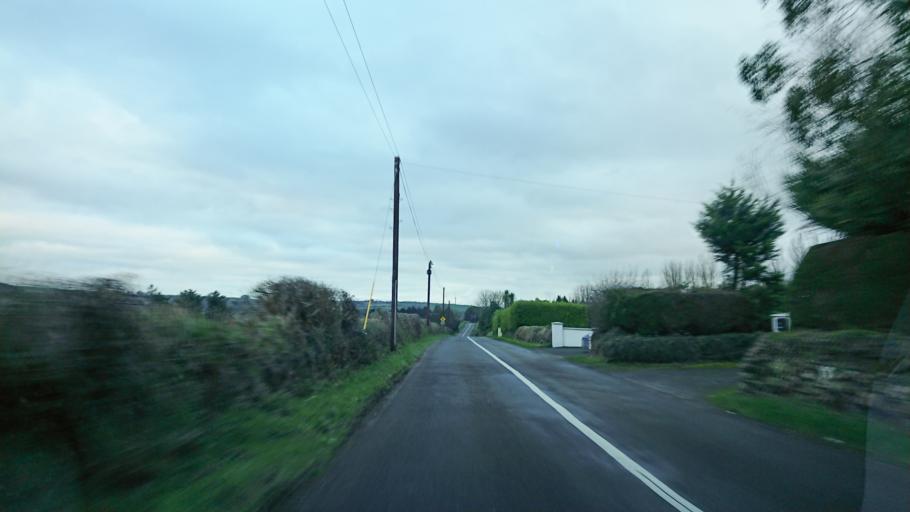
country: IE
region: Munster
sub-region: Waterford
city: Portlaw
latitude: 52.1959
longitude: -7.4239
